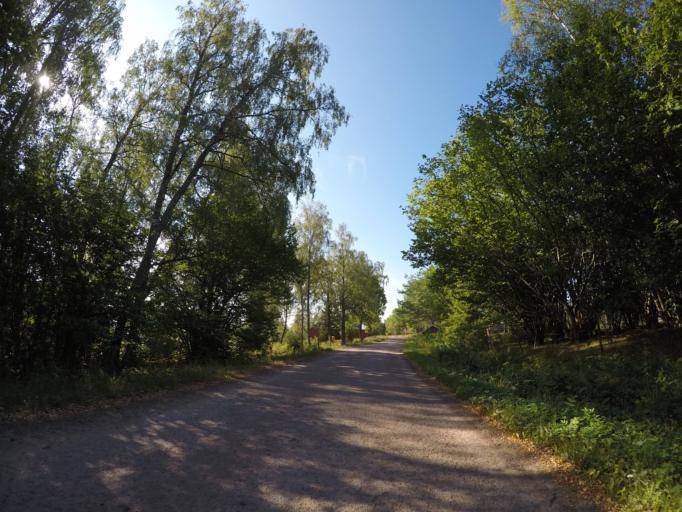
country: AX
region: Alands landsbygd
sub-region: Finstroem
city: Finstroem
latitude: 60.2482
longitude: 19.9218
